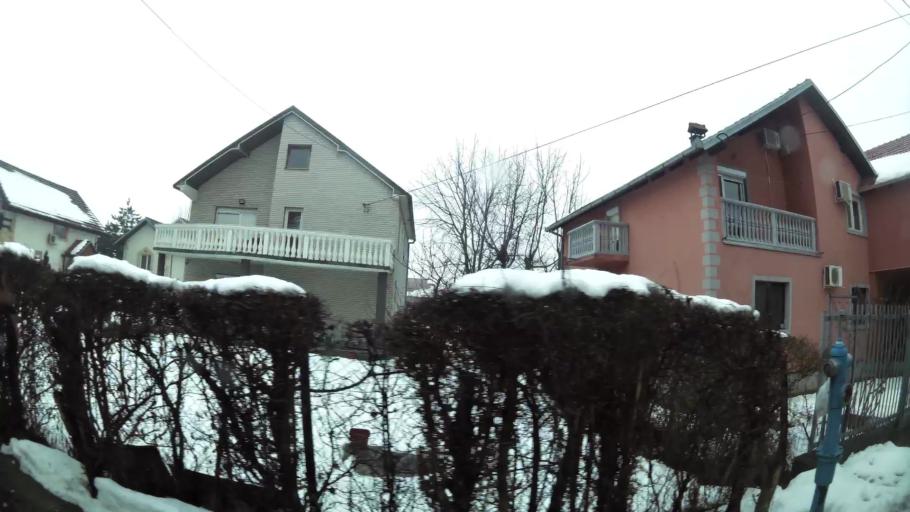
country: RS
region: Central Serbia
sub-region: Belgrade
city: Zemun
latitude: 44.8430
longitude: 20.3613
